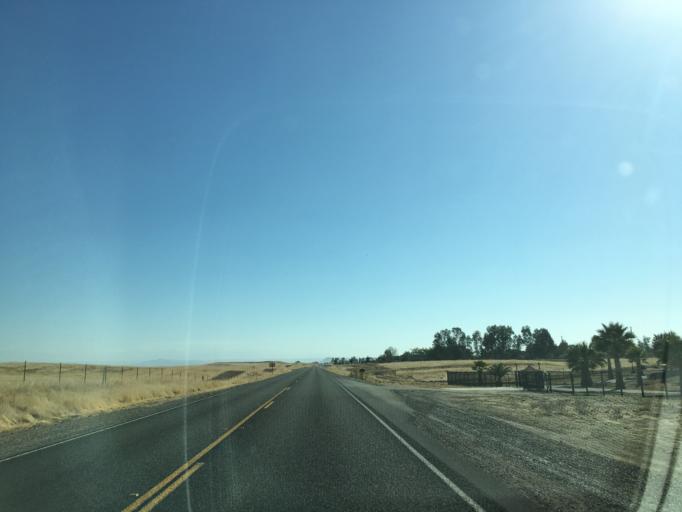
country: US
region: California
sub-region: Madera County
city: Bonadelle Ranchos-Madera Ranchos
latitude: 37.0104
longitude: -119.8842
